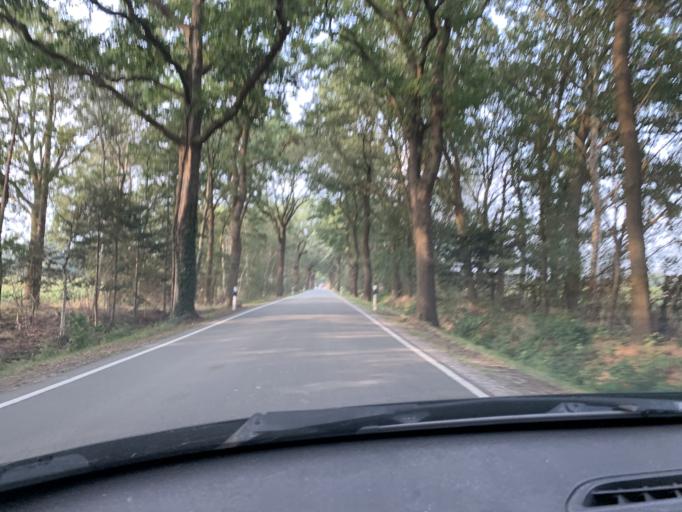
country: DE
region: Lower Saxony
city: Apen
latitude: 53.2015
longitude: 7.7933
